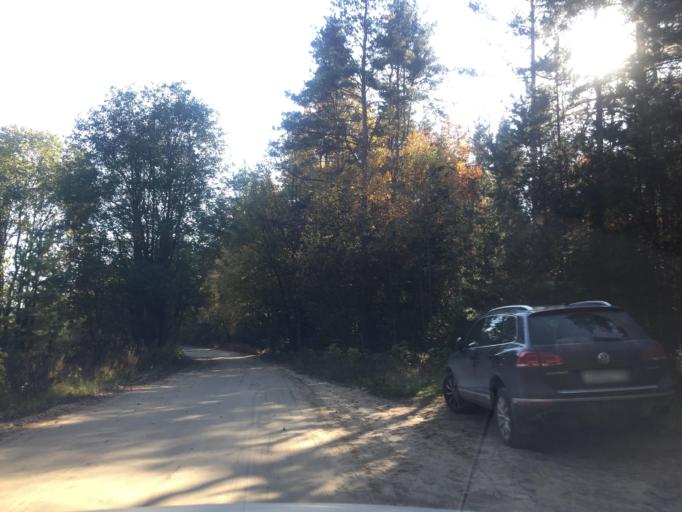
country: RU
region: Leningrad
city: Kuznechnoye
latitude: 61.2992
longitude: 30.0571
